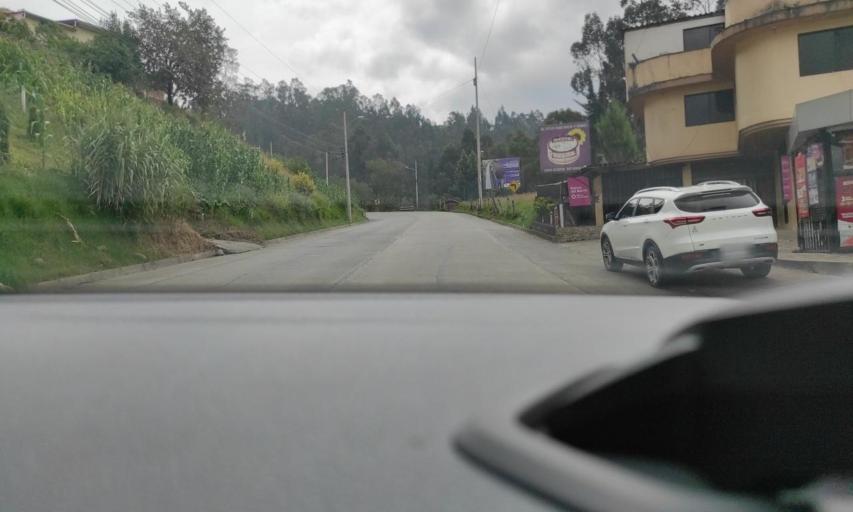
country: EC
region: Canar
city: Azogues
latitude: -2.7046
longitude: -78.8904
